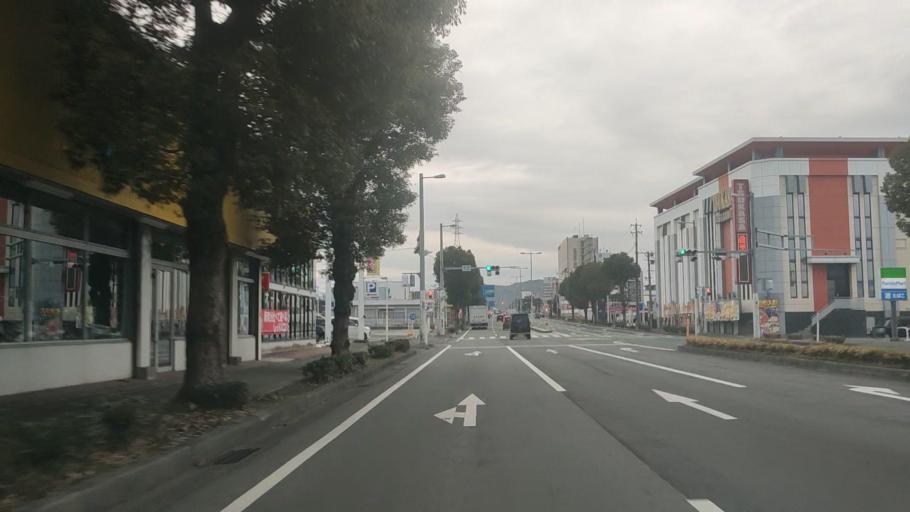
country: JP
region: Kumamoto
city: Kumamoto
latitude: 32.8276
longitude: 130.7673
